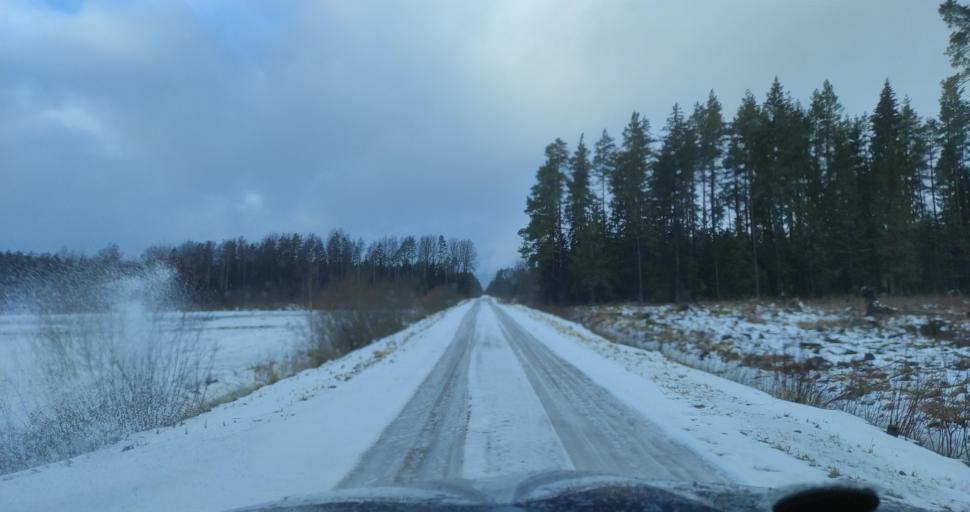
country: LV
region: Dundaga
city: Dundaga
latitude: 57.4032
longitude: 22.1009
